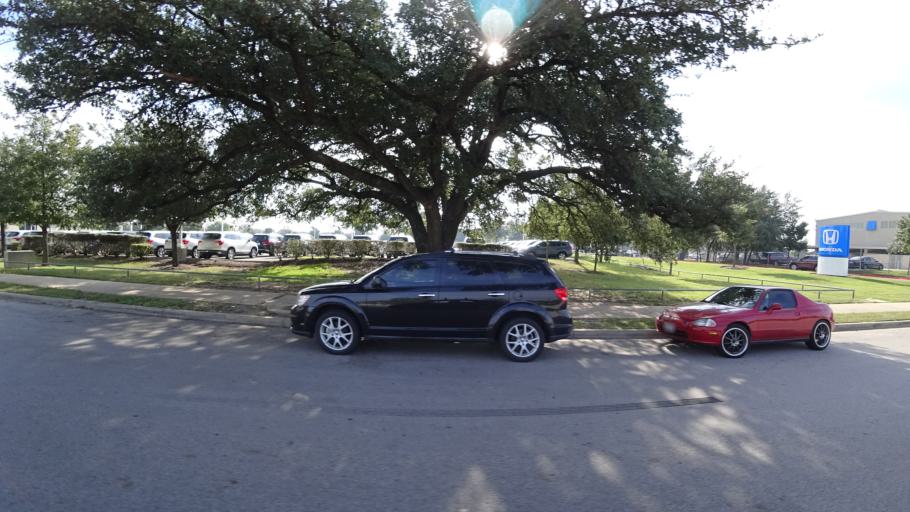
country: US
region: Texas
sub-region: Travis County
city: Austin
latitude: 30.2120
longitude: -97.7240
